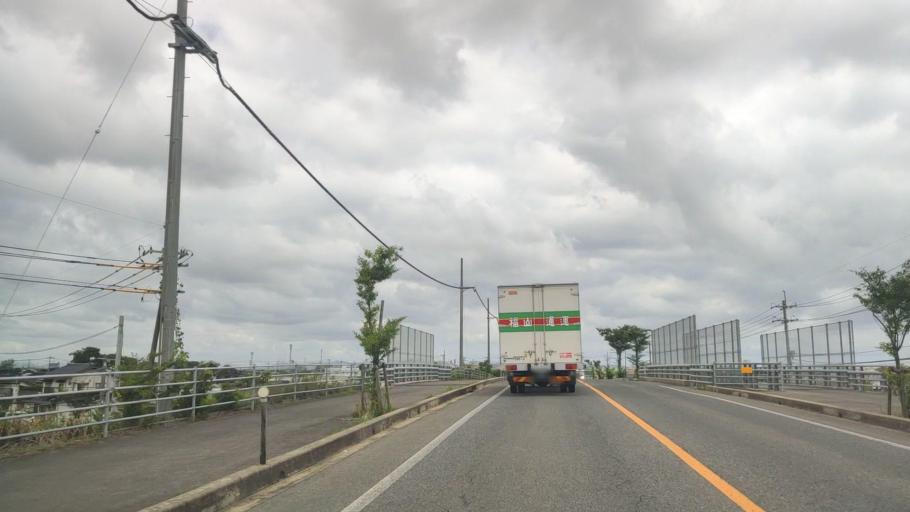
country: JP
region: Tottori
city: Yonago
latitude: 35.4335
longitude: 133.3913
